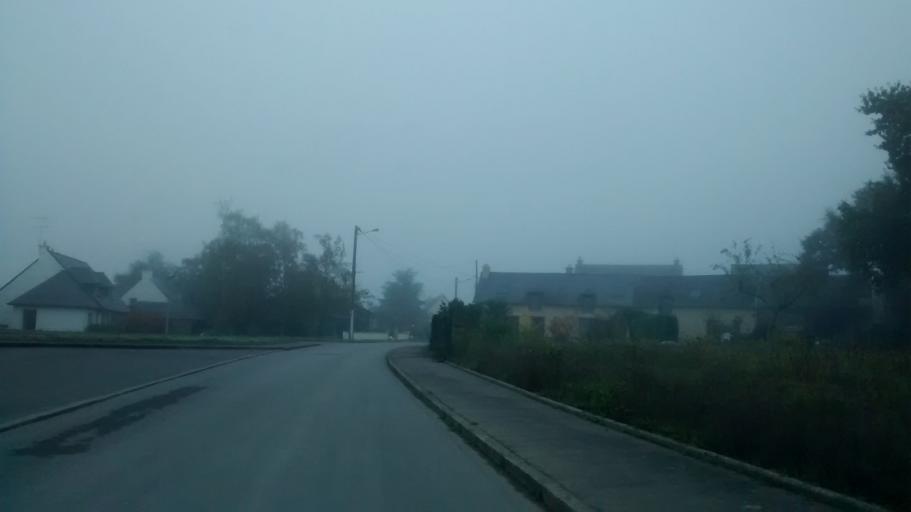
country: FR
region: Brittany
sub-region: Departement d'Ille-et-Vilaine
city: Liffre
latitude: 48.2069
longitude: -1.5036
